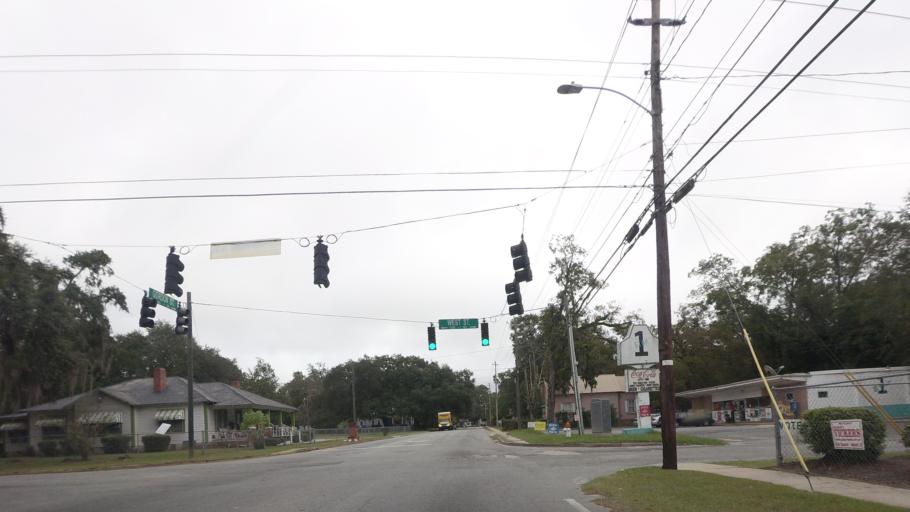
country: US
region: Georgia
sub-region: Lowndes County
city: Valdosta
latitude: 30.8374
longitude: -83.2908
